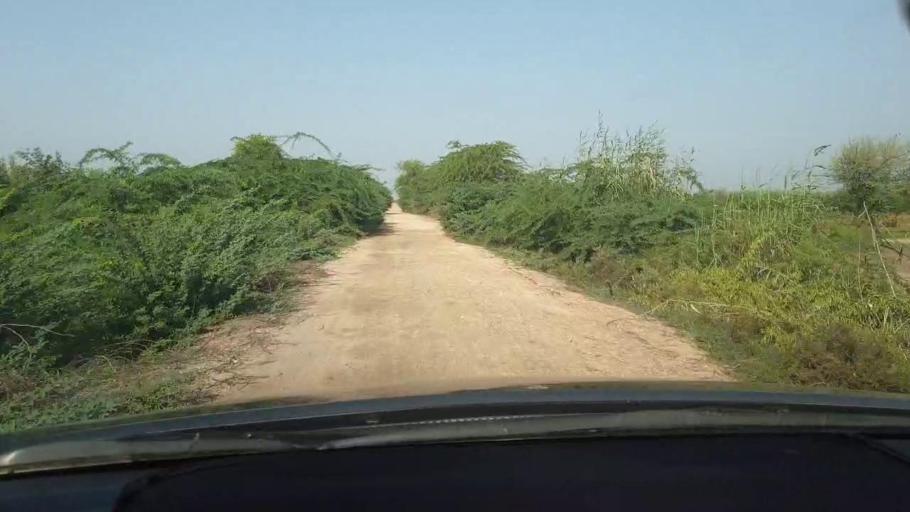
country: PK
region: Sindh
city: Tando Bago
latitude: 24.6800
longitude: 69.1393
